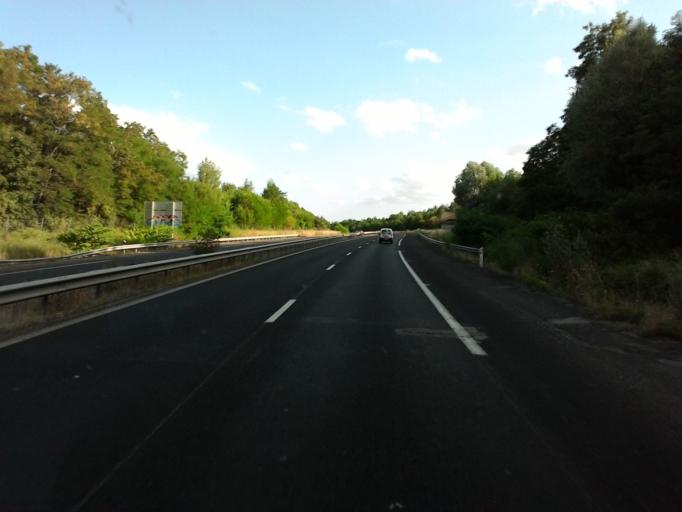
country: FR
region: Lorraine
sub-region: Departement de Meurthe-et-Moselle
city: Flavigny-sur-Moselle
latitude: 48.5681
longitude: 6.1759
